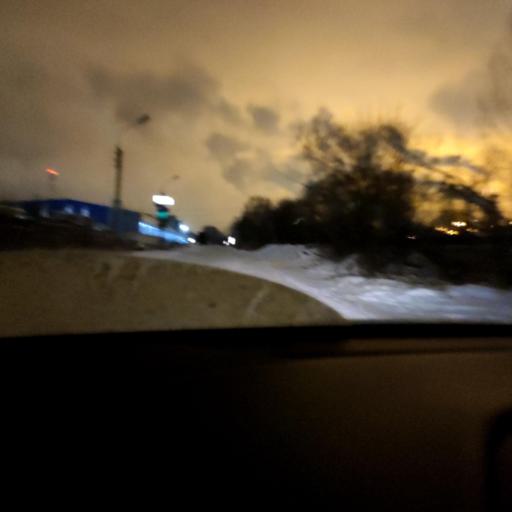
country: RU
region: Tatarstan
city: Staroye Arakchino
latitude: 55.8609
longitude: 48.9742
